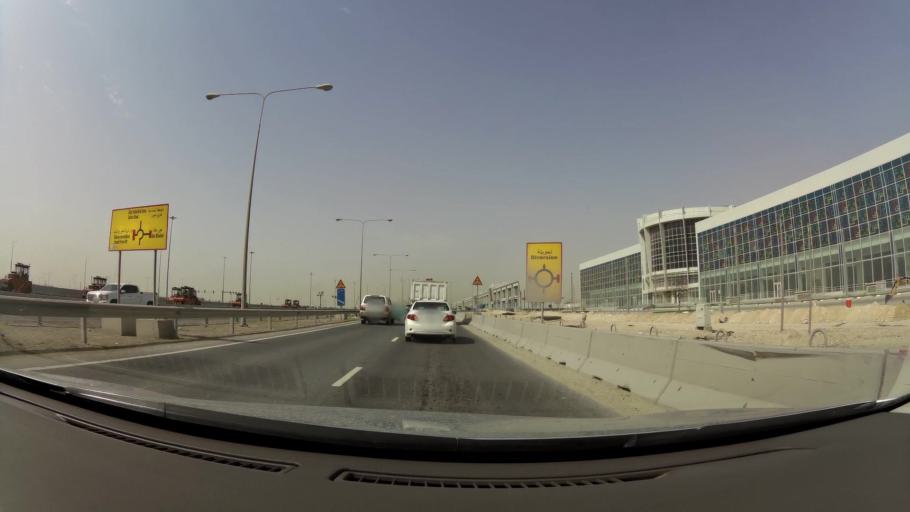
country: QA
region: Al Wakrah
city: Al Wukayr
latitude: 25.2026
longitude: 51.4775
